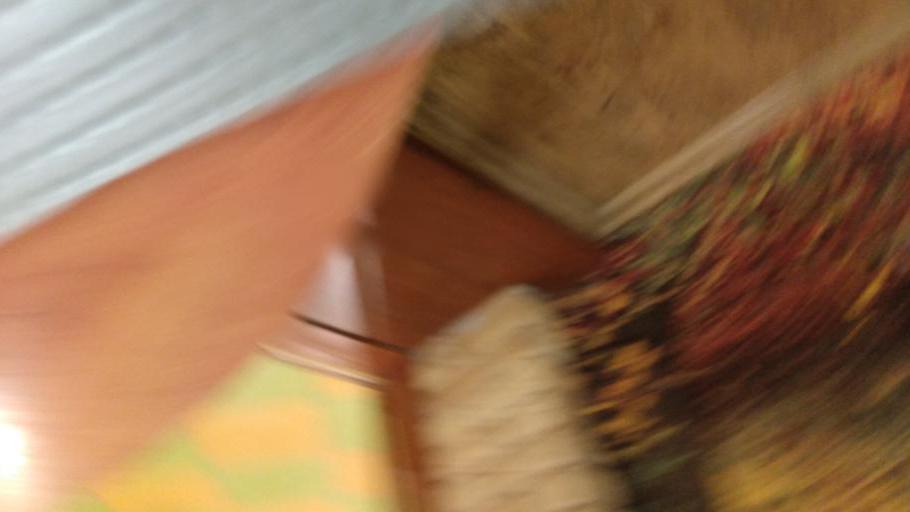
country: RU
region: Vologda
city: Babayevo
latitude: 59.3747
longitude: 35.9917
